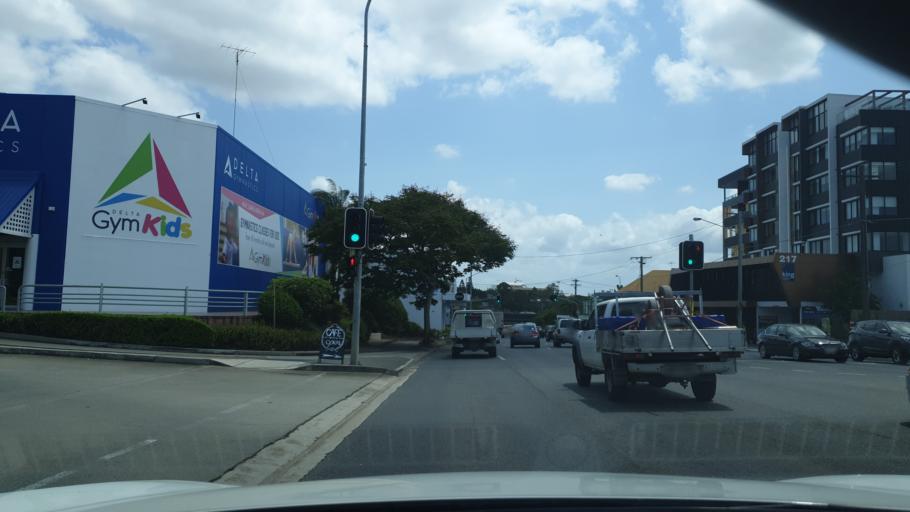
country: AU
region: Queensland
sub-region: Brisbane
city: Windsor
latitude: -27.4364
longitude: 153.0312
